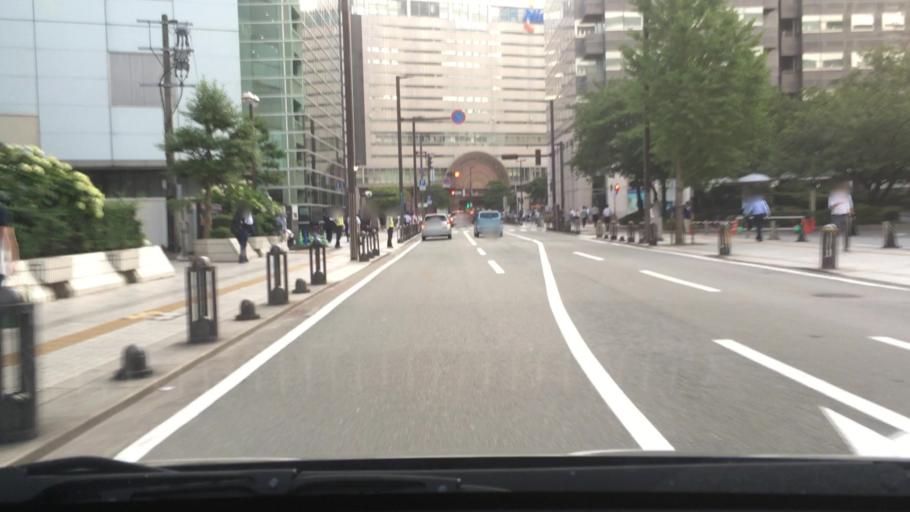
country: JP
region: Fukuoka
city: Fukuoka-shi
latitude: 33.5895
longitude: 130.4018
